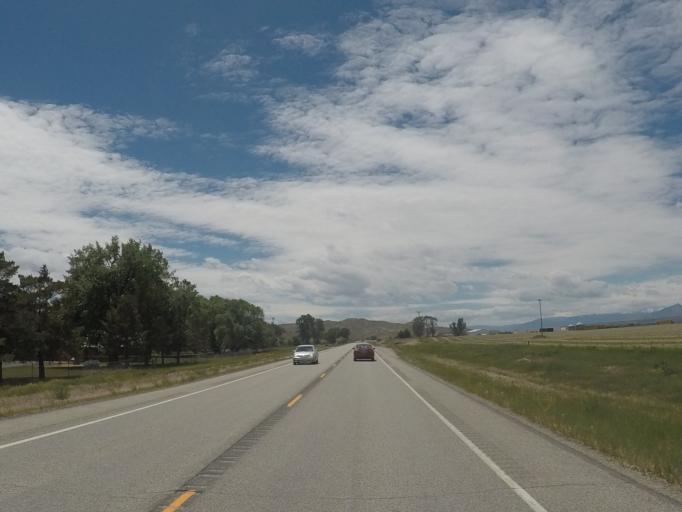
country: US
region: Montana
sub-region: Carbon County
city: Red Lodge
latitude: 45.0925
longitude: -109.0279
